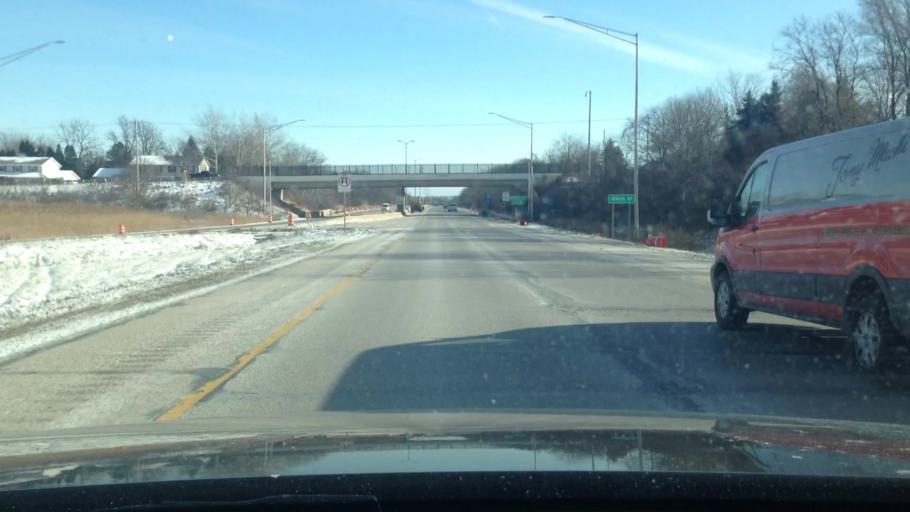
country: US
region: Wisconsin
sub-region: Milwaukee County
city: Hales Corners
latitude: 42.9575
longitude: -88.0711
